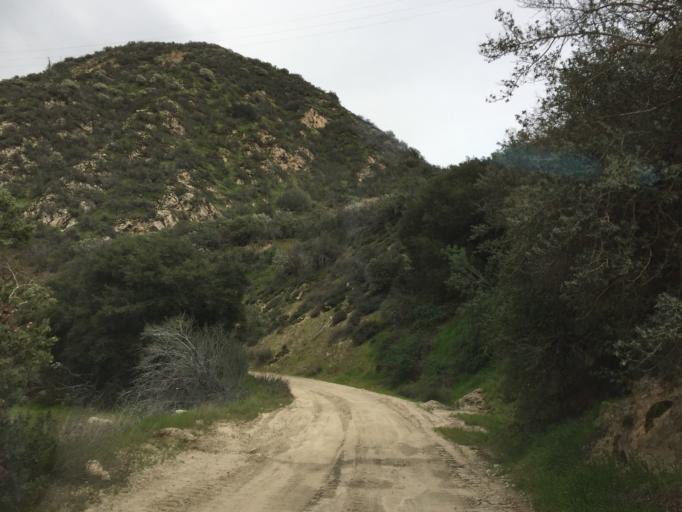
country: US
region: California
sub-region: San Bernardino County
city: Running Springs
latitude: 34.1351
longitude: -117.0721
